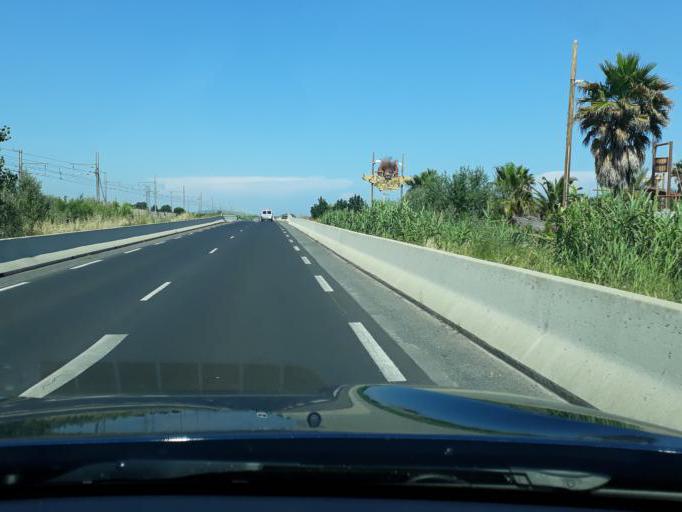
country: FR
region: Languedoc-Roussillon
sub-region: Departement de l'Herault
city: Marseillan
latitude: 43.3235
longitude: 3.5469
